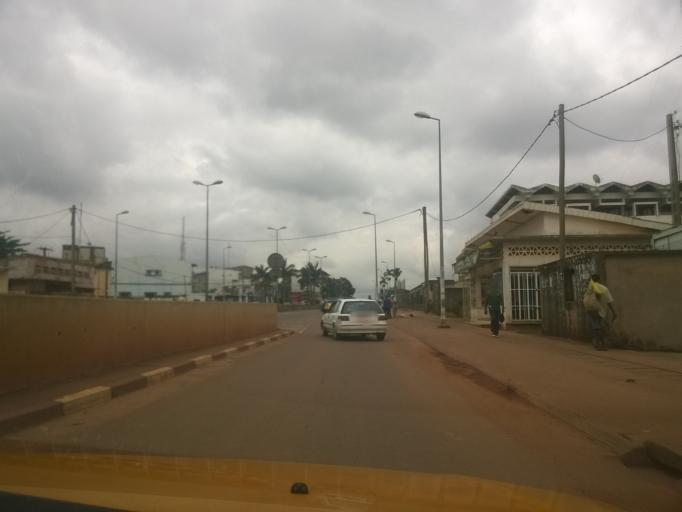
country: CM
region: Centre
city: Yaounde
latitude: 3.8797
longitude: 11.5161
